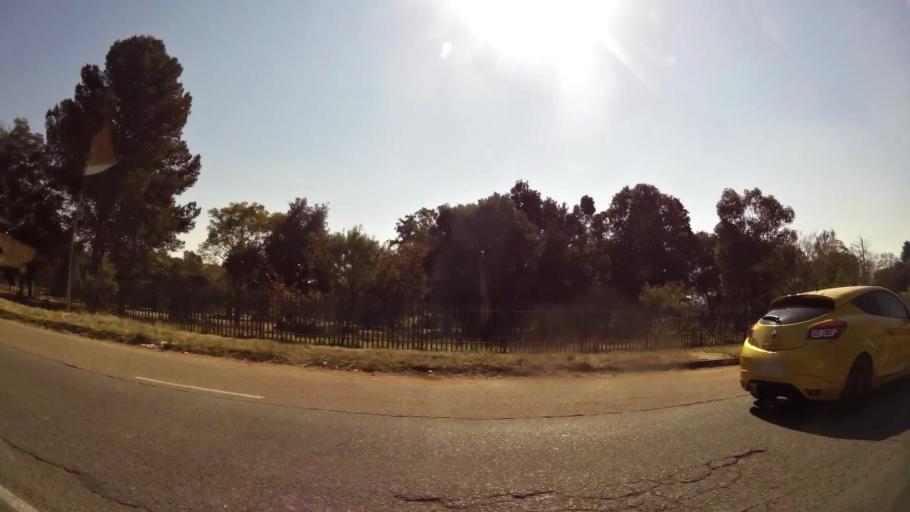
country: ZA
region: Gauteng
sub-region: City of Johannesburg Metropolitan Municipality
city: Johannesburg
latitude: -26.1623
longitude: 28.1123
